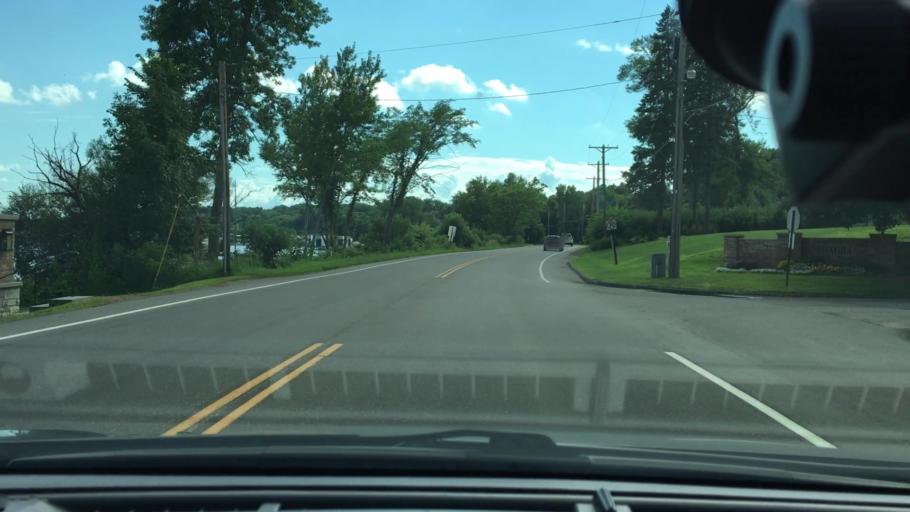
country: US
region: Minnesota
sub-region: Hennepin County
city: Long Lake
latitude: 44.9559
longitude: -93.5688
